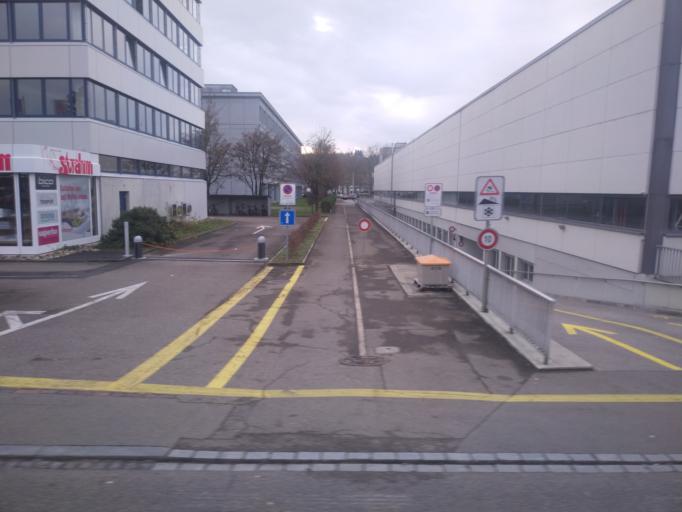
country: CH
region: Zurich
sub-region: Bezirk Winterthur
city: Mattenbach (Kreis 7) / Gutschick
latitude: 47.4948
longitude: 8.7554
